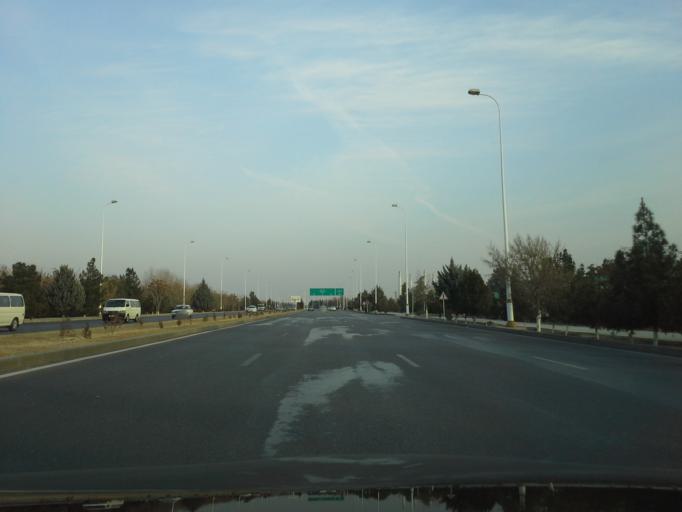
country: TM
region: Ahal
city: Abadan
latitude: 38.0268
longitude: 58.2382
